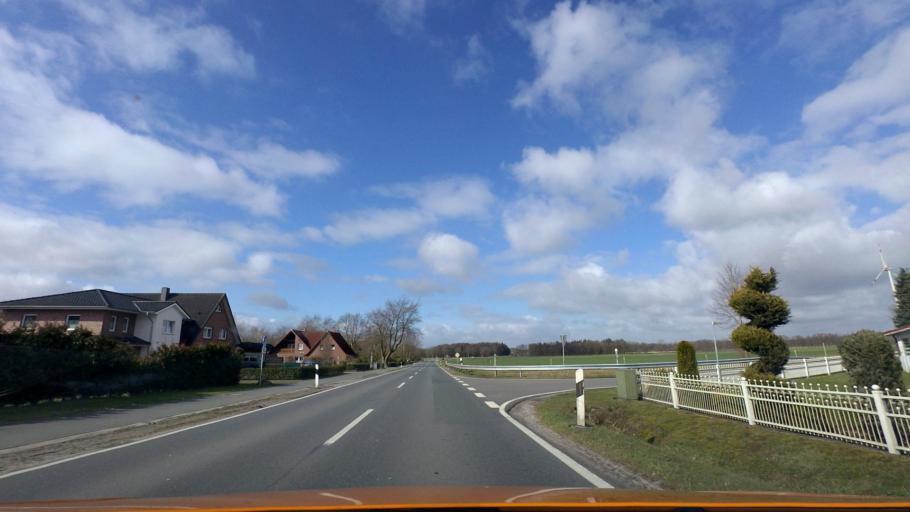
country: DE
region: Lower Saxony
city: Bosel
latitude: 53.0102
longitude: 7.9195
